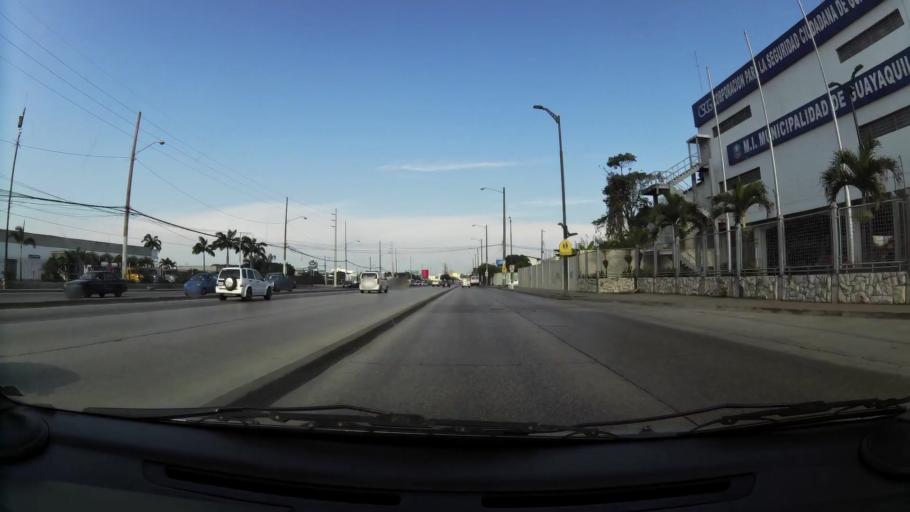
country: EC
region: Guayas
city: Guayaquil
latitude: -2.1427
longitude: -79.9216
